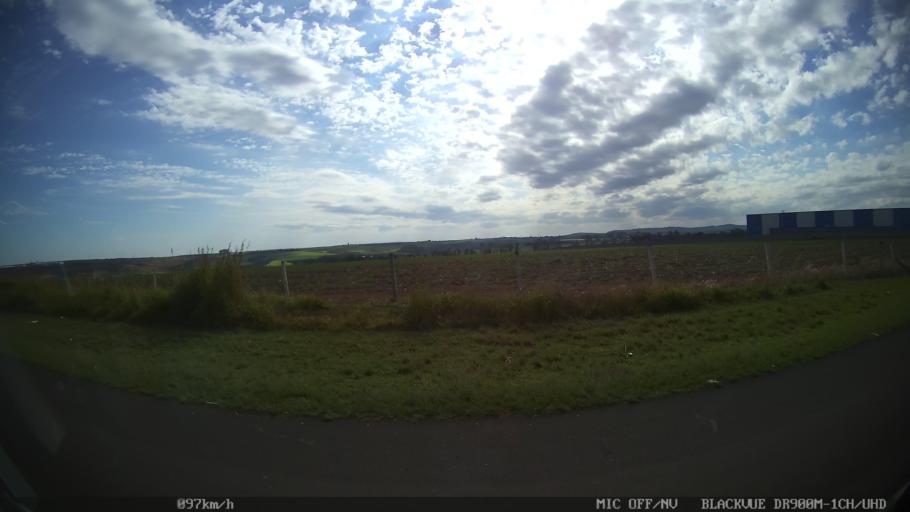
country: BR
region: Sao Paulo
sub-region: Iracemapolis
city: Iracemapolis
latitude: -22.6141
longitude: -47.4798
